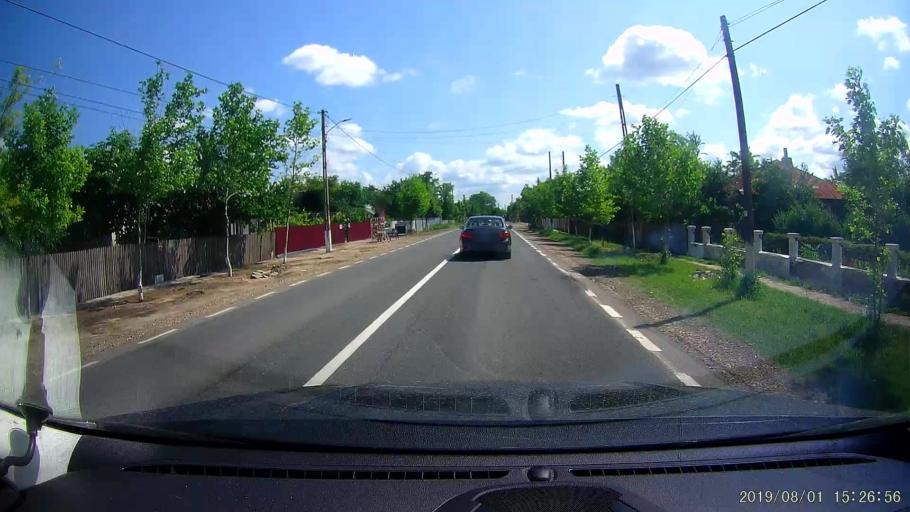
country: RO
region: Braila
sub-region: Comuna Viziru
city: Viziru
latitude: 45.0052
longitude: 27.7175
